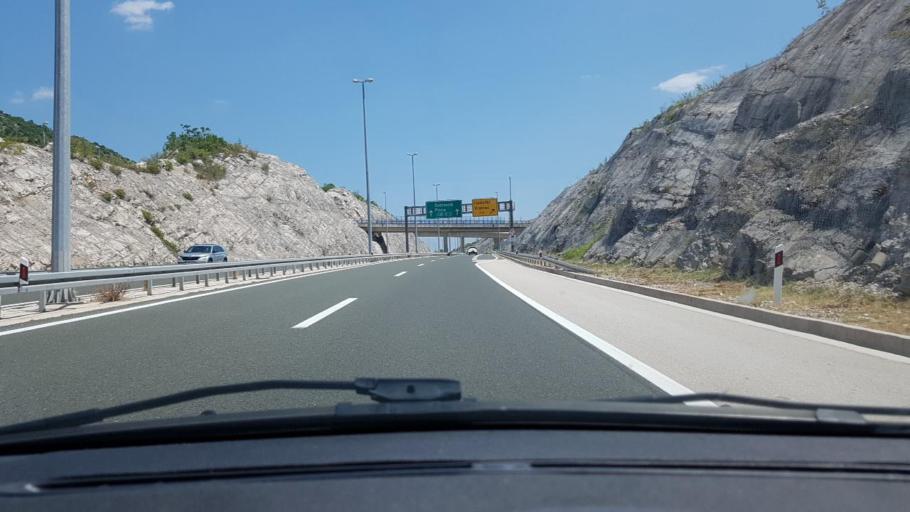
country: HR
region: Splitsko-Dalmatinska
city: Vrgorac
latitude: 43.1903
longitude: 17.3767
